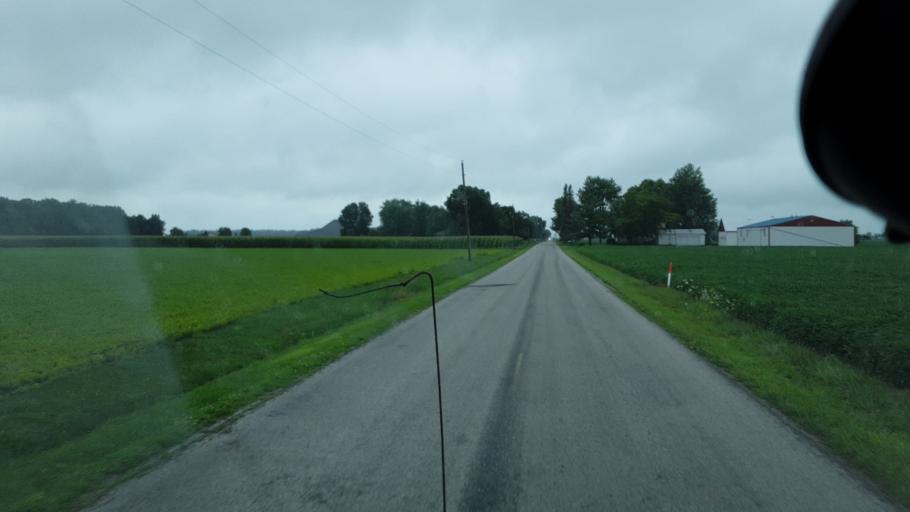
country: US
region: Indiana
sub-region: Wells County
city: Ossian
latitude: 40.8993
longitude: -85.1096
